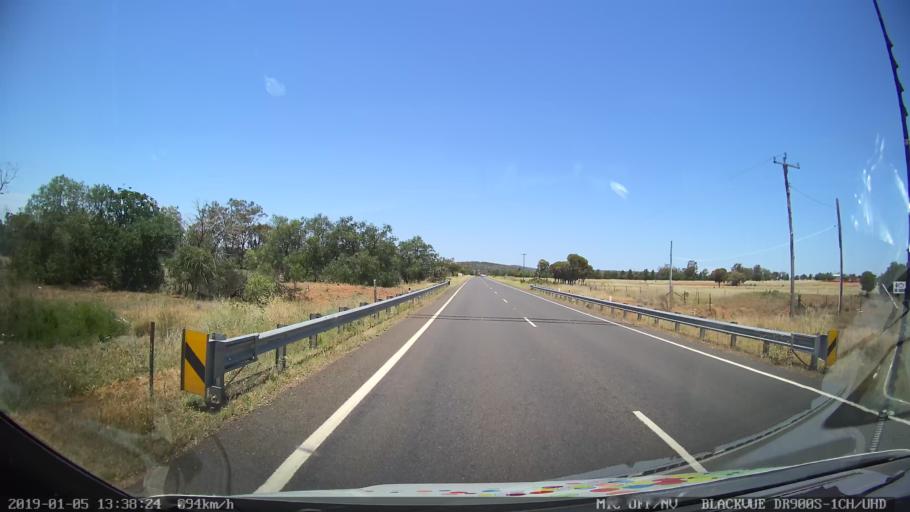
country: AU
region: New South Wales
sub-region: Gunnedah
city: Gunnedah
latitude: -30.9842
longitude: 150.1977
